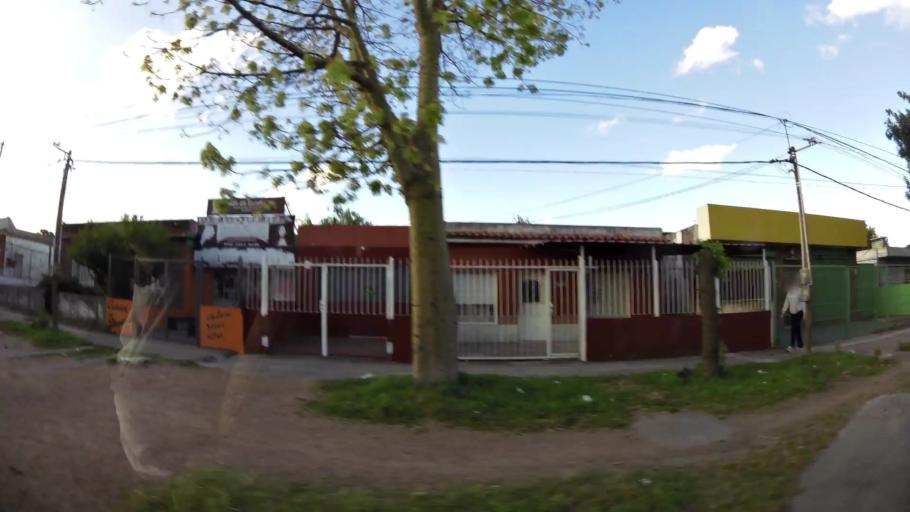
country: UY
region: Montevideo
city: Montevideo
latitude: -34.8750
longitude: -56.2580
